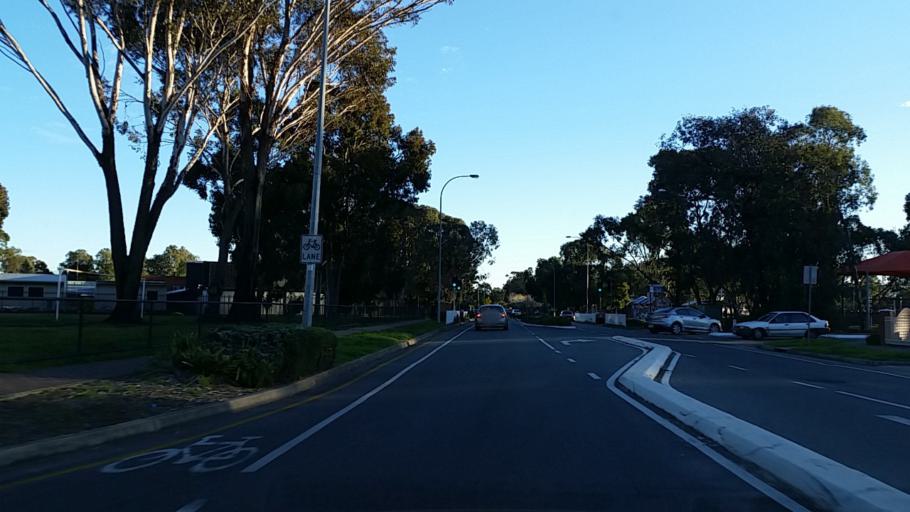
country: AU
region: South Australia
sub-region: Salisbury
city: Salisbury
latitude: -34.7518
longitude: 138.6350
